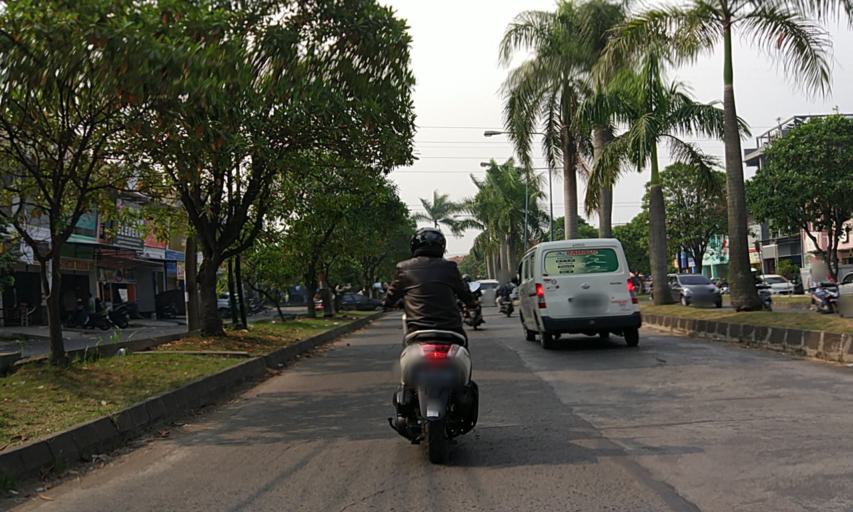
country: ID
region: West Java
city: Margahayukencana
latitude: -6.9589
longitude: 107.5607
